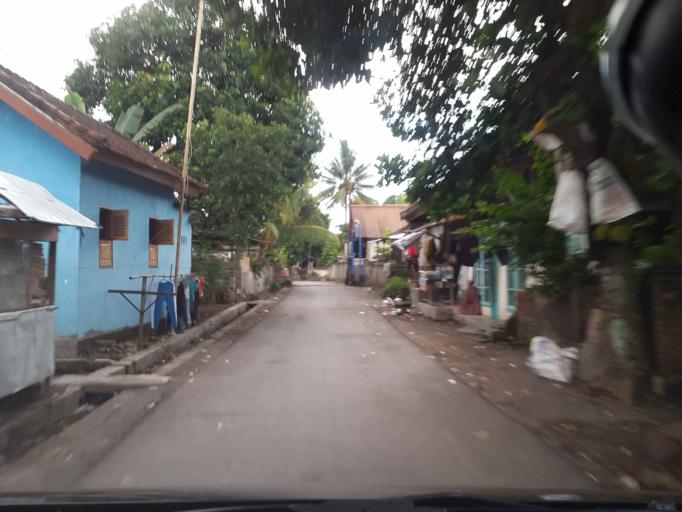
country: ID
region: West Nusa Tenggara
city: Karangkebon Timur
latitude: -8.6391
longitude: 116.1384
